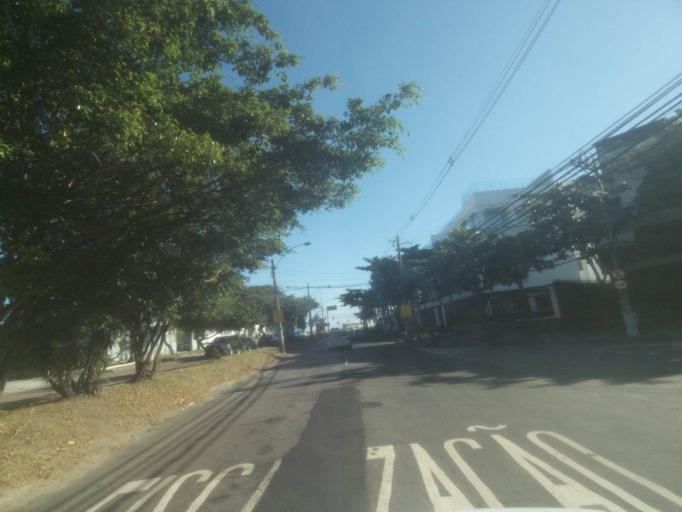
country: BR
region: Rio de Janeiro
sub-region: Rio De Janeiro
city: Rio de Janeiro
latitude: -23.0131
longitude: -43.3124
